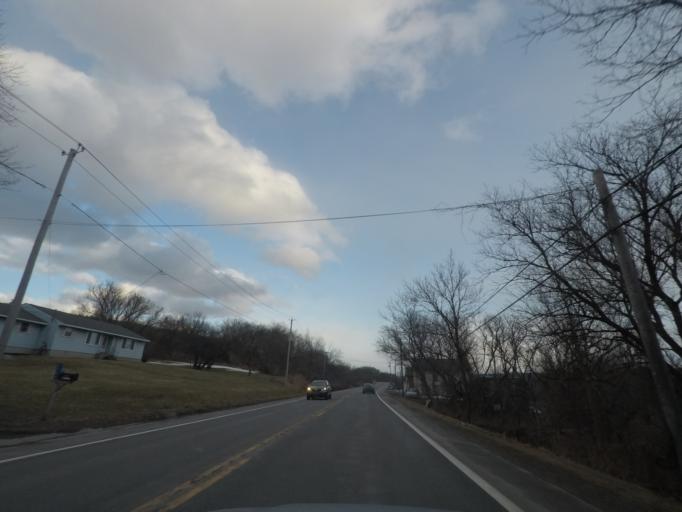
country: US
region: New York
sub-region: Herkimer County
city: Frankfort
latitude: 43.0479
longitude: -75.0652
